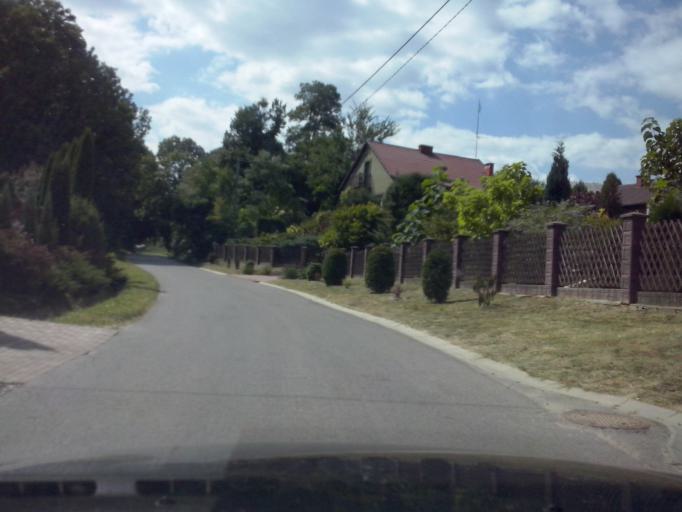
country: PL
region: Swietokrzyskie
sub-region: Powiat staszowski
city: Staszow
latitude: 50.5671
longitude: 21.1270
